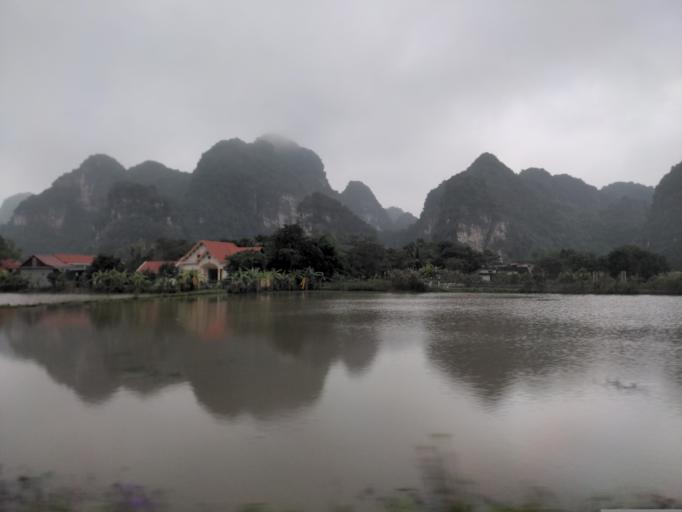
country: VN
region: Ninh Binh
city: Thi Tran Tam Diep
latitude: 20.2093
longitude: 105.9090
